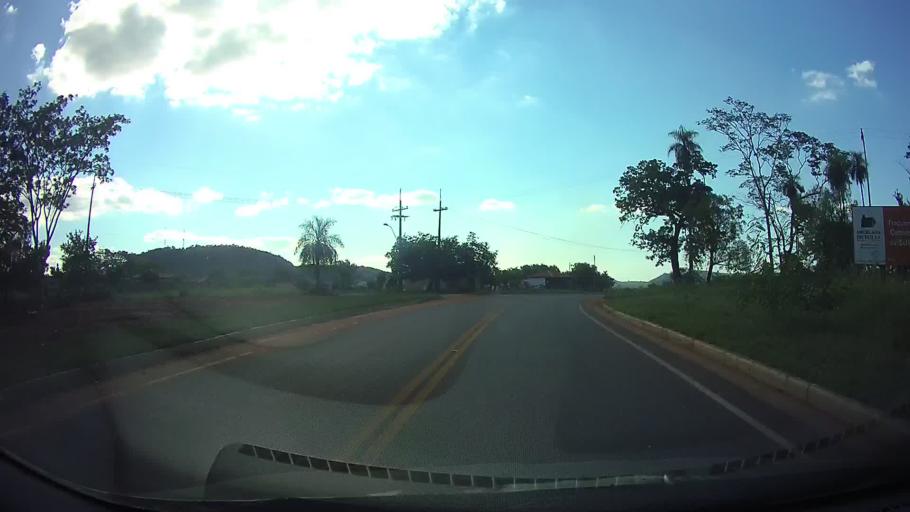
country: PY
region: Cordillera
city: Caacupe
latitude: -25.3675
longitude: -57.1436
